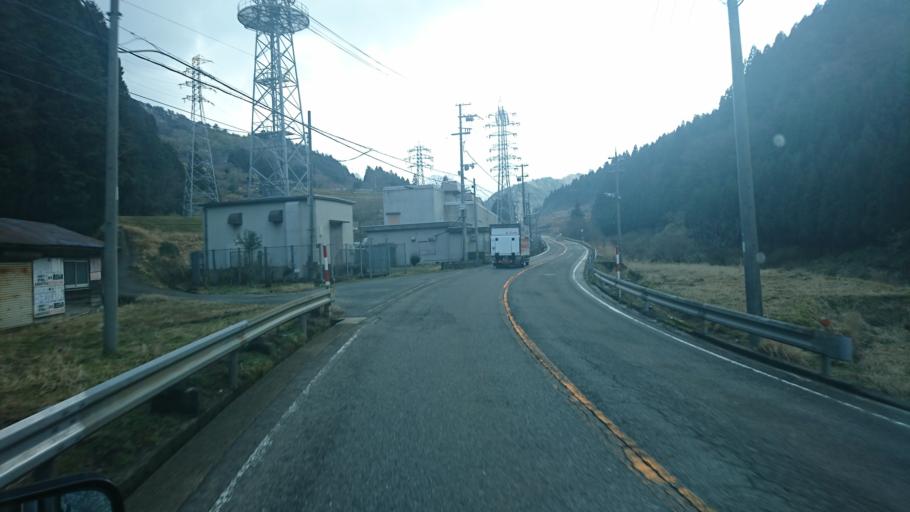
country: JP
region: Tottori
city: Tottori
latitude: 35.5431
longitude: 134.5061
